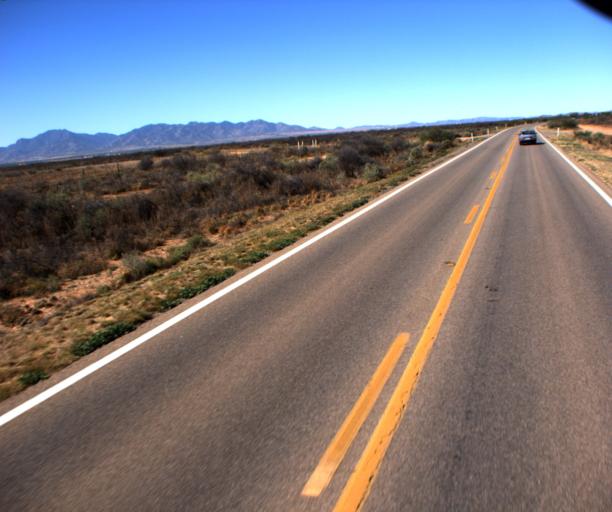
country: US
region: Arizona
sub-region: Cochise County
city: Huachuca City
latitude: 31.6975
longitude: -110.3036
